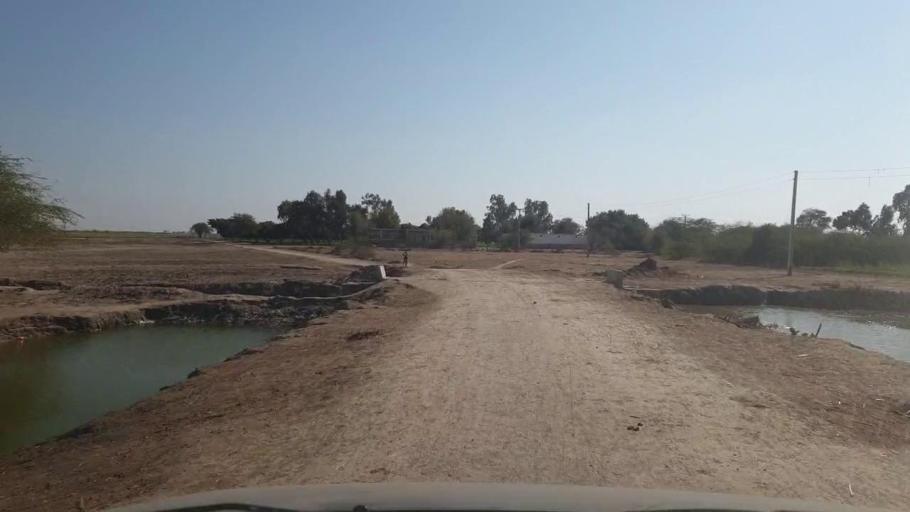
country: PK
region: Sindh
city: Samaro
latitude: 25.3658
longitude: 69.3215
